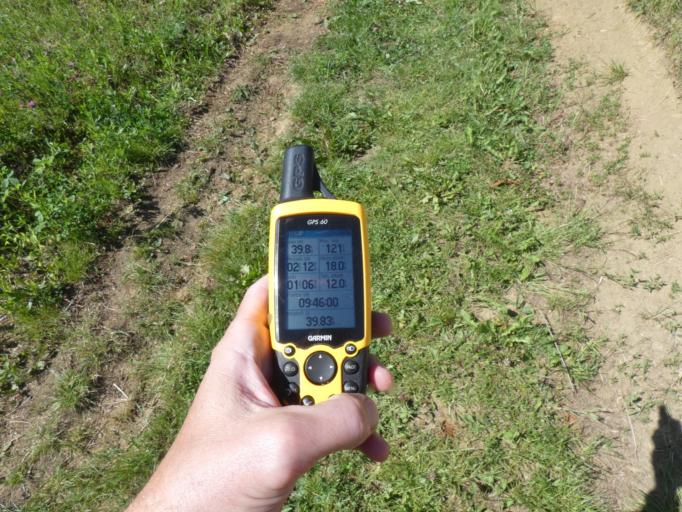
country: HU
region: Heves
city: Petervasara
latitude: 48.0598
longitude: 20.1102
